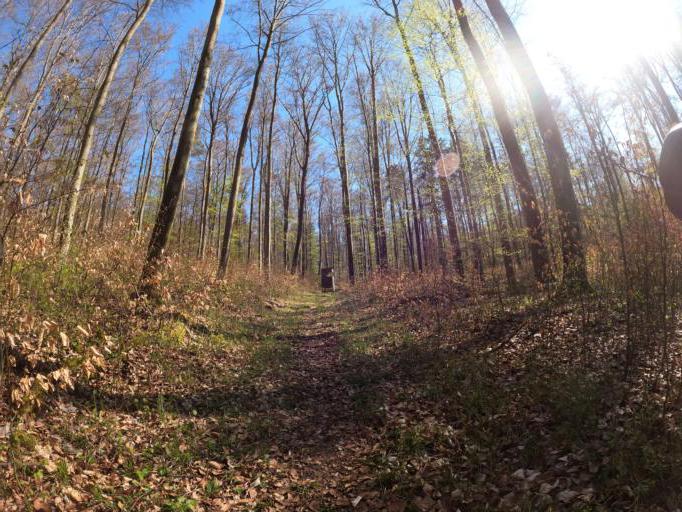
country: DE
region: Baden-Wuerttemberg
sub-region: Karlsruhe Region
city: Monsheim
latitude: 48.9041
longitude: 8.9047
